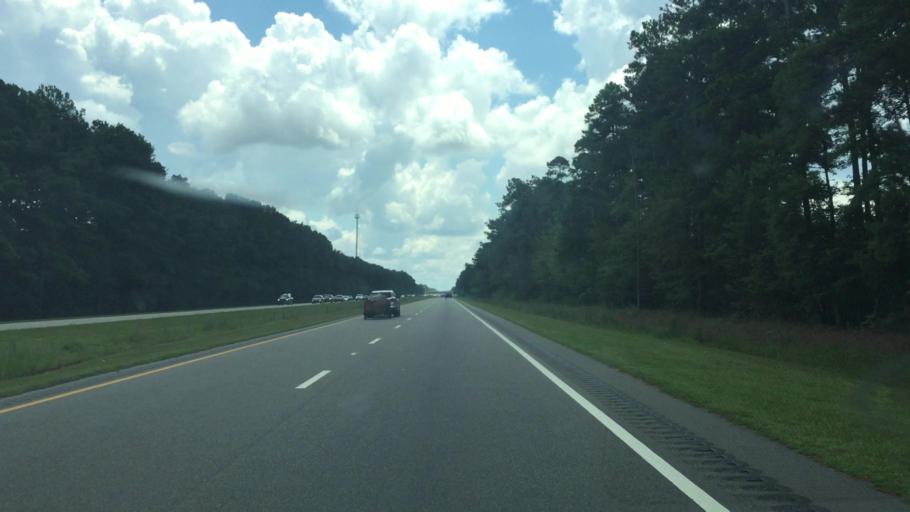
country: US
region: North Carolina
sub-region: Columbus County
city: Chadbourn
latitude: 34.3738
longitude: -78.8451
